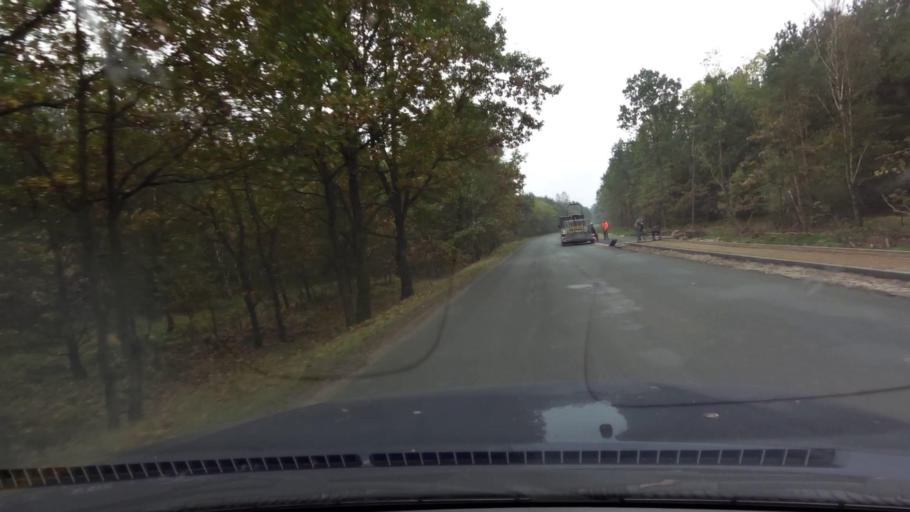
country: PL
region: West Pomeranian Voivodeship
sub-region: Powiat goleniowski
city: Goleniow
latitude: 53.5377
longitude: 14.7649
